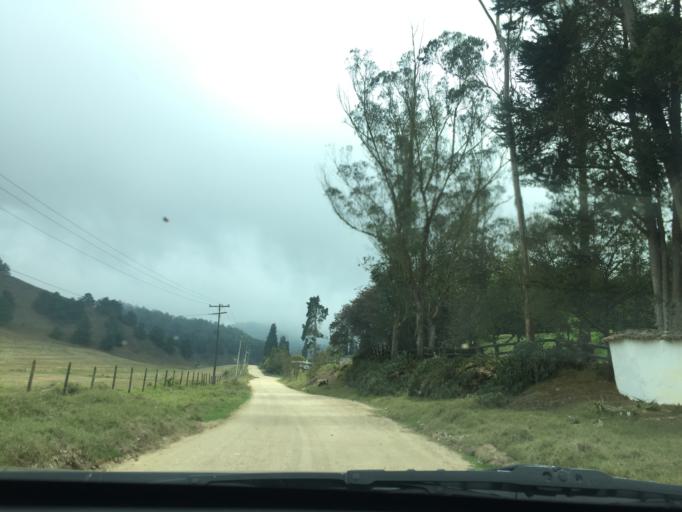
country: CO
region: Cundinamarca
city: Bojaca
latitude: 4.6835
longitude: -74.3190
